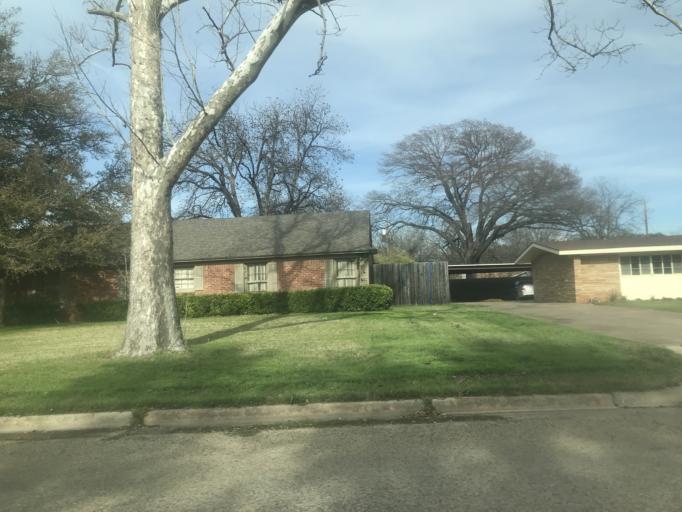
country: US
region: Texas
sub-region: Taylor County
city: Abilene
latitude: 32.4312
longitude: -99.7712
